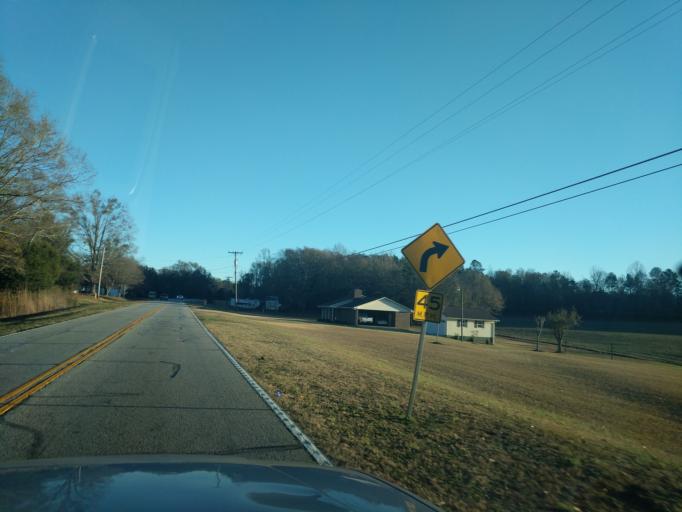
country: US
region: Georgia
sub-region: Hart County
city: Reed Creek
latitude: 34.5528
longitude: -82.8672
